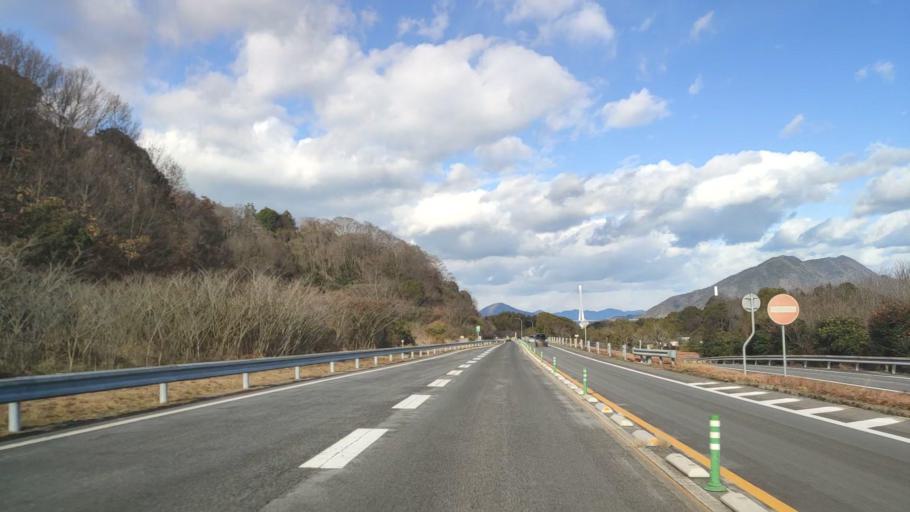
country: JP
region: Hiroshima
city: Innoshima
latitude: 34.2279
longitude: 133.0466
